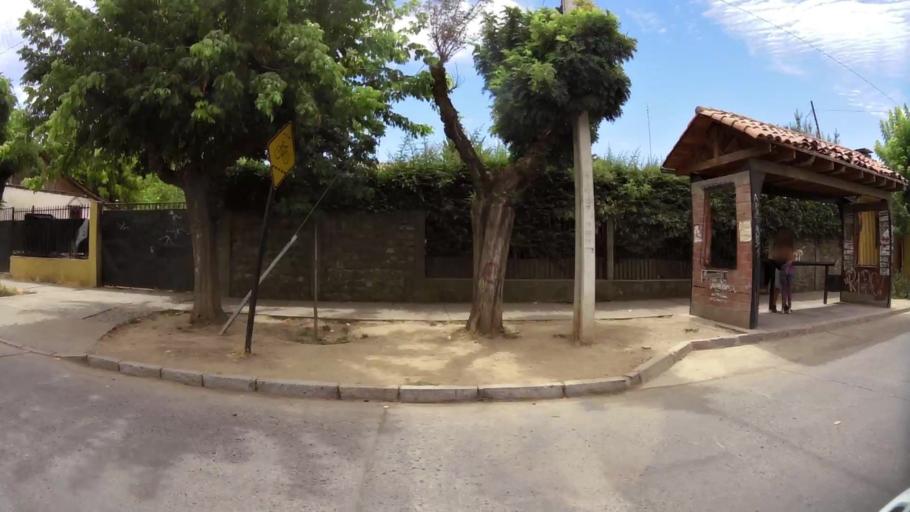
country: CL
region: O'Higgins
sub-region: Provincia de Cachapoal
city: Graneros
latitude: -34.0668
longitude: -70.7312
